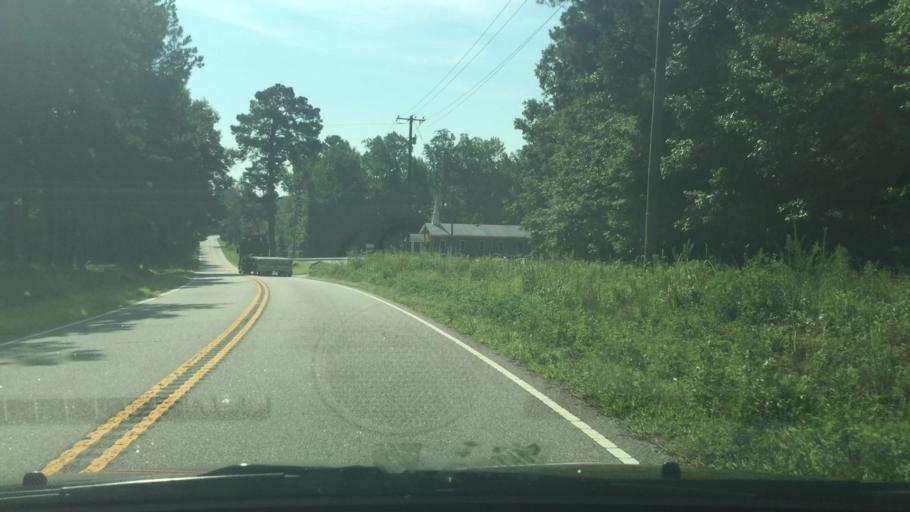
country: US
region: Virginia
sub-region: Sussex County
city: Sussex
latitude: 37.0144
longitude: -77.2795
